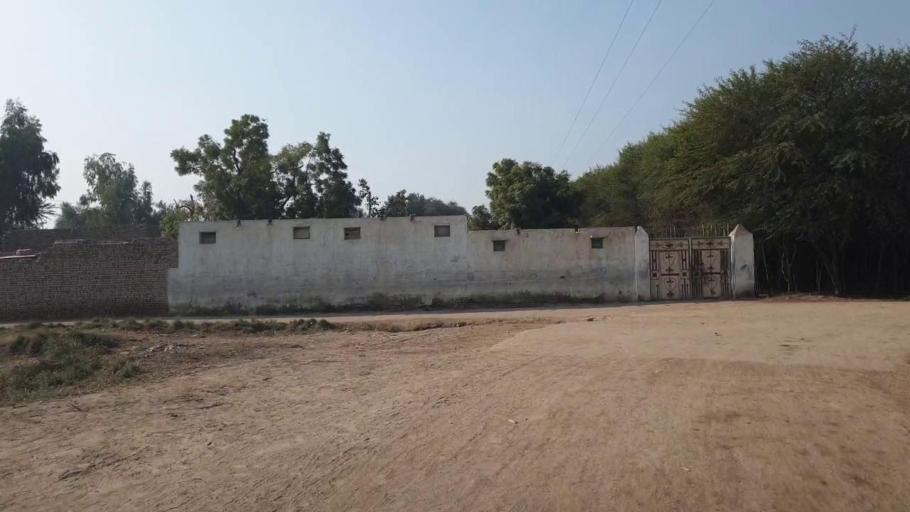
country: PK
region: Sindh
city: Matiari
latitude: 25.6747
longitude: 68.4958
